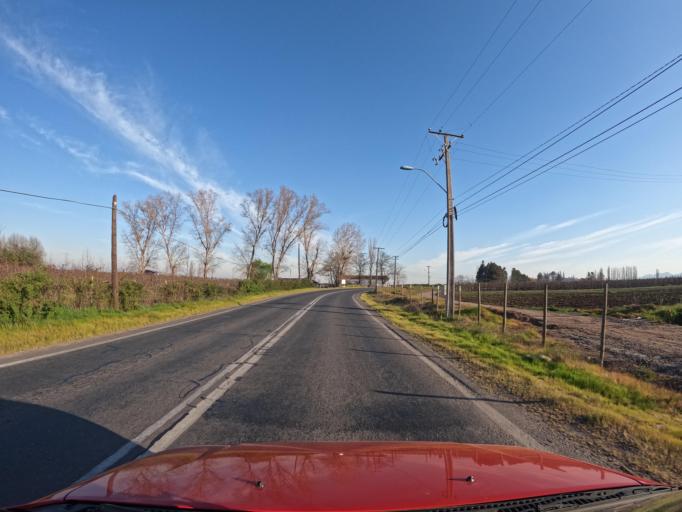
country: CL
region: Maule
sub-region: Provincia de Curico
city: Rauco
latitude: -34.8985
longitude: -71.2735
